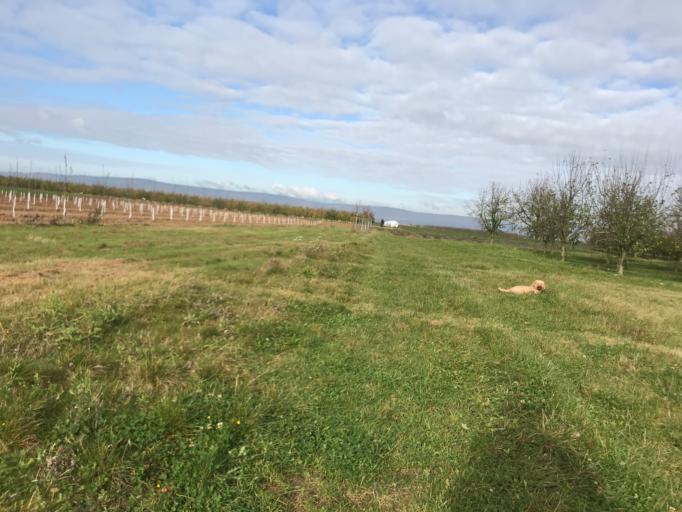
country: DE
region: Rheinland-Pfalz
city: Wackernheim
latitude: 49.9826
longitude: 8.1514
